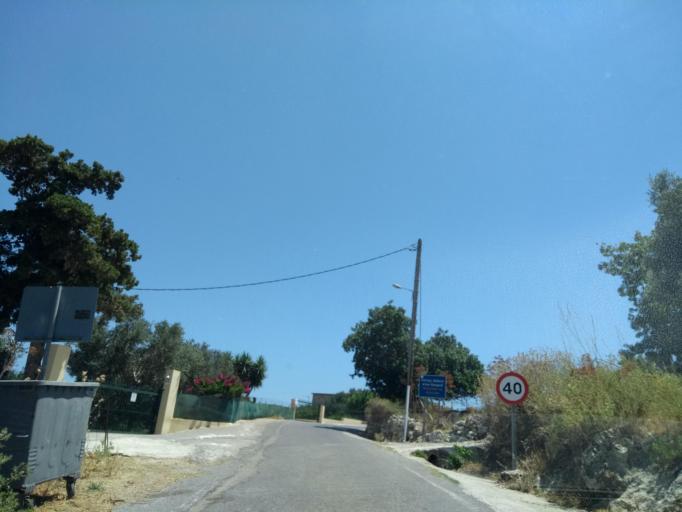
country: GR
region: Crete
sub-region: Nomos Chanias
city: Georgioupolis
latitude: 35.3161
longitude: 24.2917
